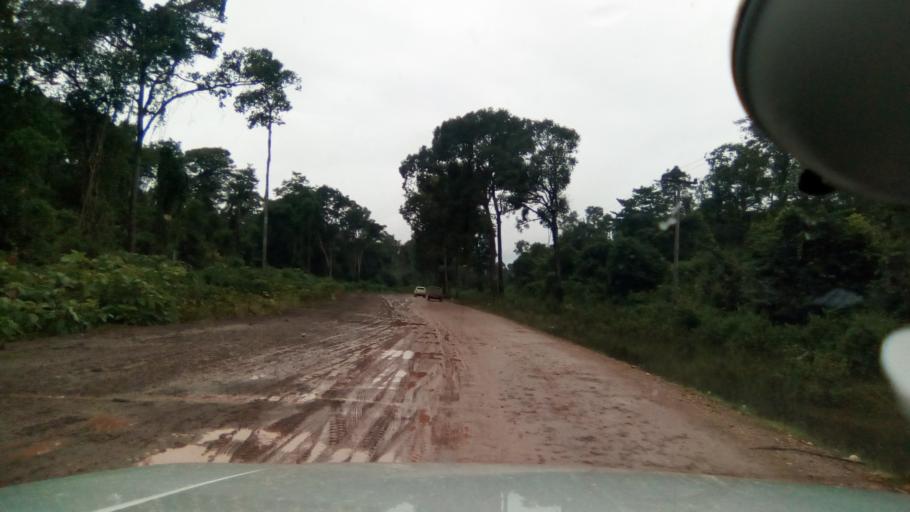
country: LA
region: Attapu
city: Attapu
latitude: 14.6801
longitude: 106.5582
